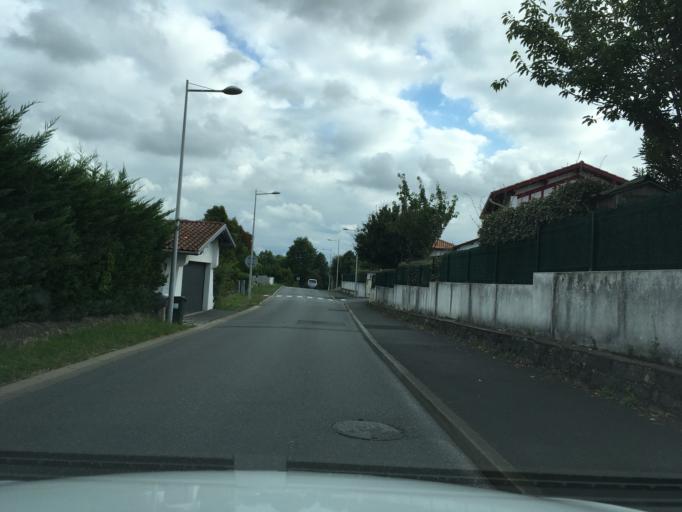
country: FR
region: Aquitaine
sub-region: Departement des Pyrenees-Atlantiques
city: Anglet
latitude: 43.4585
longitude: -1.4969
